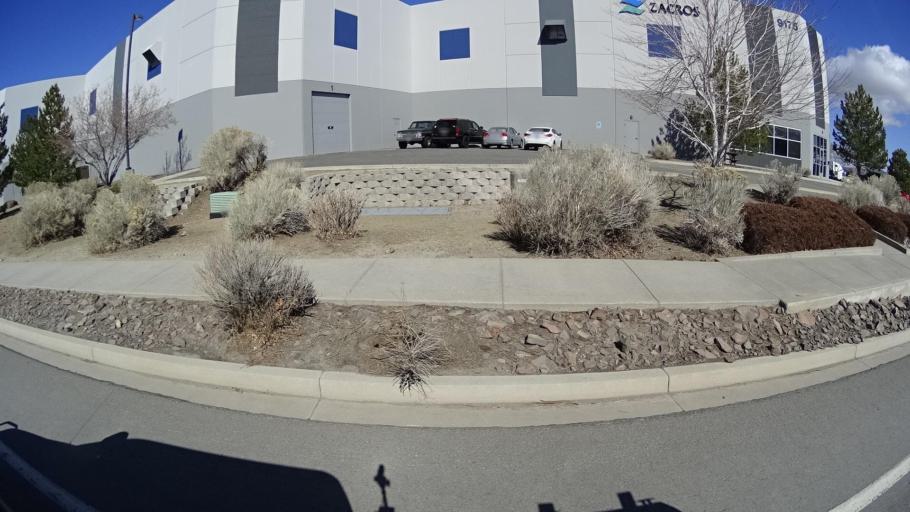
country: US
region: Nevada
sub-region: Washoe County
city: Lemmon Valley
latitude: 39.6335
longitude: -119.9117
